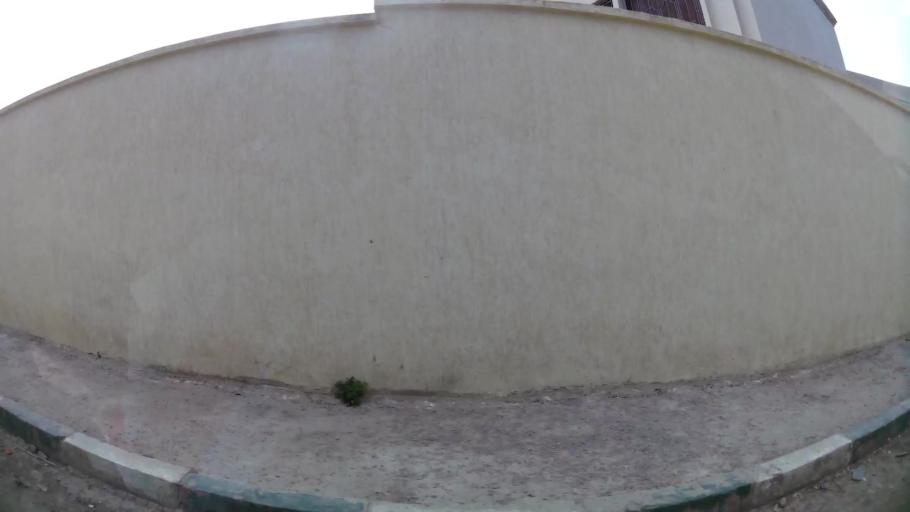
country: MA
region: Tanger-Tetouan
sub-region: Tanger-Assilah
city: Boukhalef
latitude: 35.7076
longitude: -5.9002
